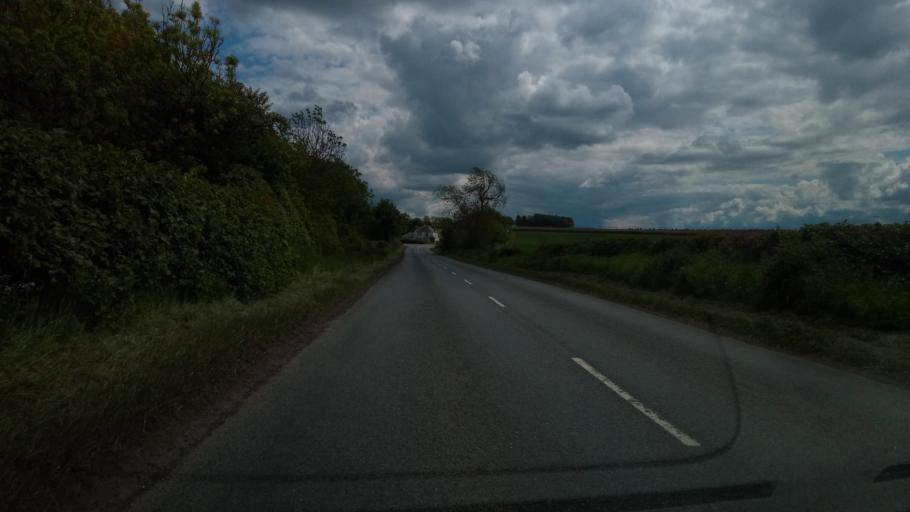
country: GB
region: Scotland
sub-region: The Scottish Borders
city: Kelso
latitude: 55.5800
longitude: -2.4087
